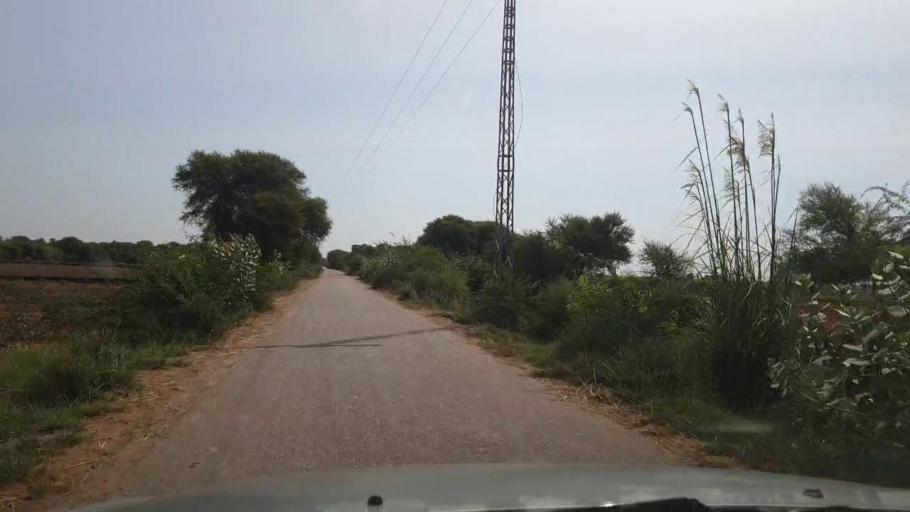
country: PK
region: Sindh
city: Tando Muhammad Khan
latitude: 25.1443
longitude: 68.4006
